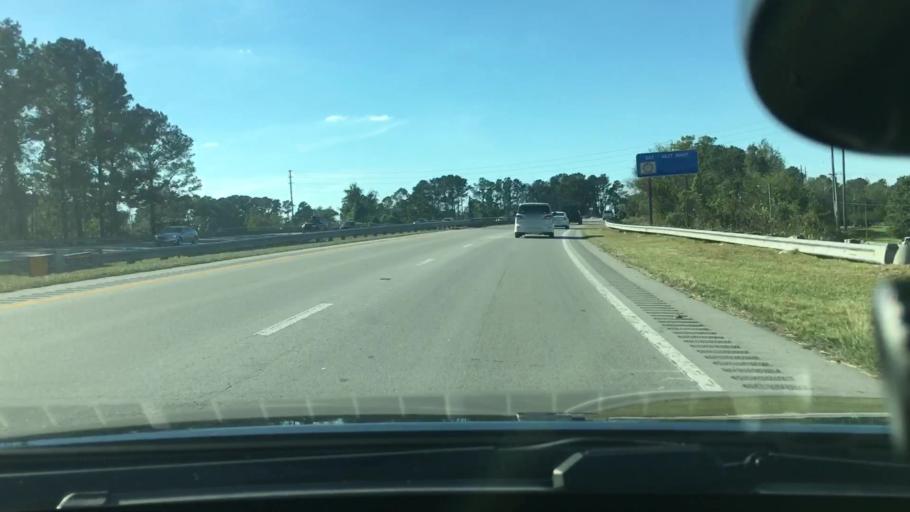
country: US
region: North Carolina
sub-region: Craven County
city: Trent Woods
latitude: 35.1000
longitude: -77.0770
